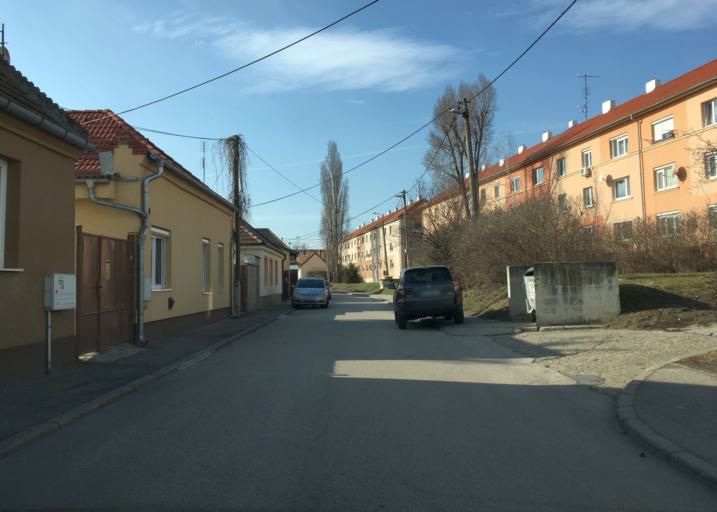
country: SK
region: Nitriansky
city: Komarno
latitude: 47.7668
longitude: 18.1280
